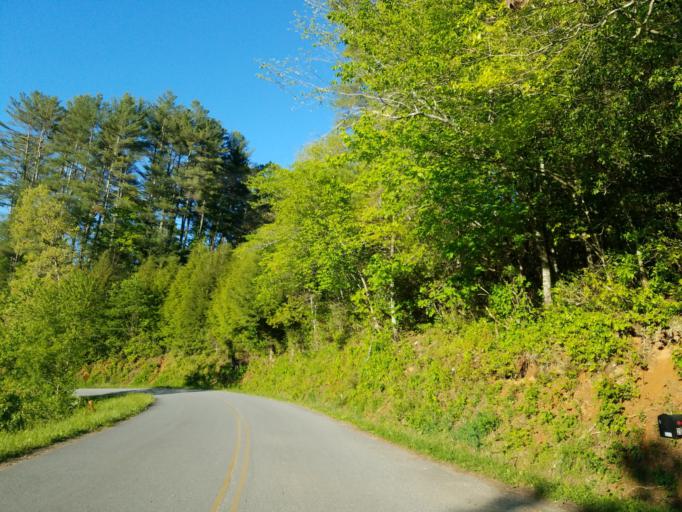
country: US
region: Georgia
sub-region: Fannin County
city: Blue Ridge
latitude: 34.7660
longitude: -84.2646
